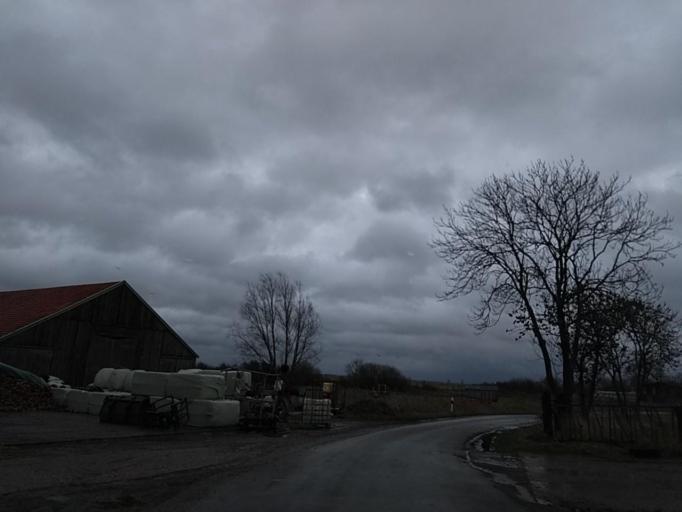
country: DE
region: Lower Saxony
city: Emden
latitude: 53.2889
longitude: 7.2618
